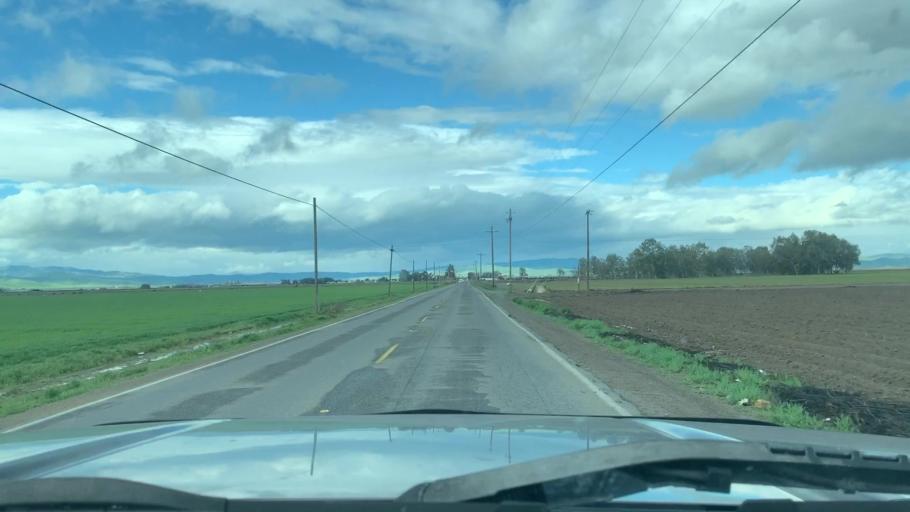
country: US
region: California
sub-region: Merced County
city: Los Banos
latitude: 37.1000
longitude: -120.8885
